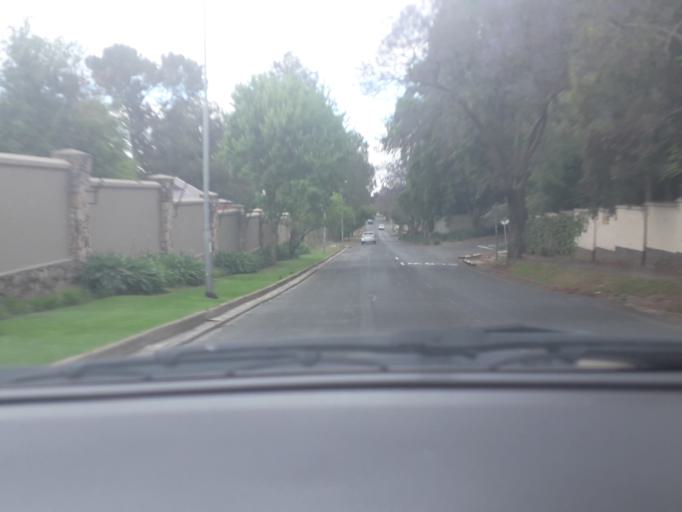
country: ZA
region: Gauteng
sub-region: City of Johannesburg Metropolitan Municipality
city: Johannesburg
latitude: -26.1685
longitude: 28.0182
